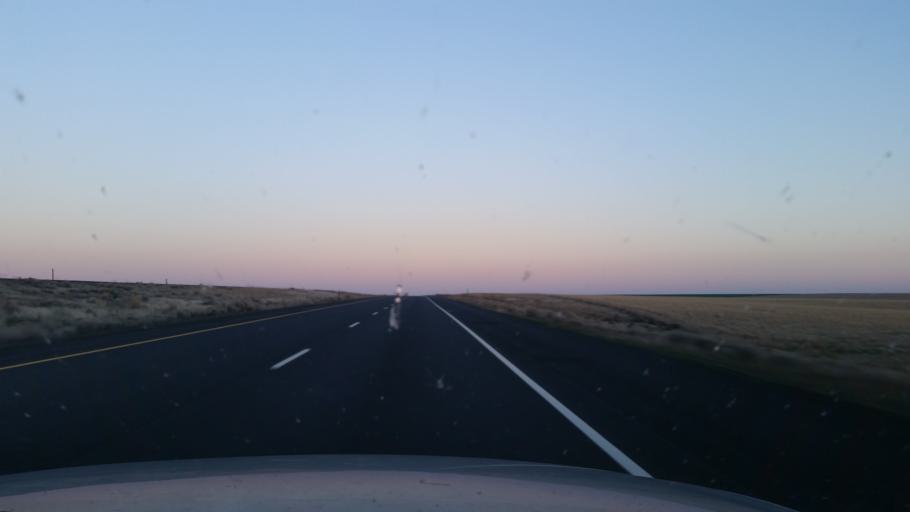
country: US
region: Washington
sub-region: Grant County
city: Warden
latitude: 47.0861
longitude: -118.7274
